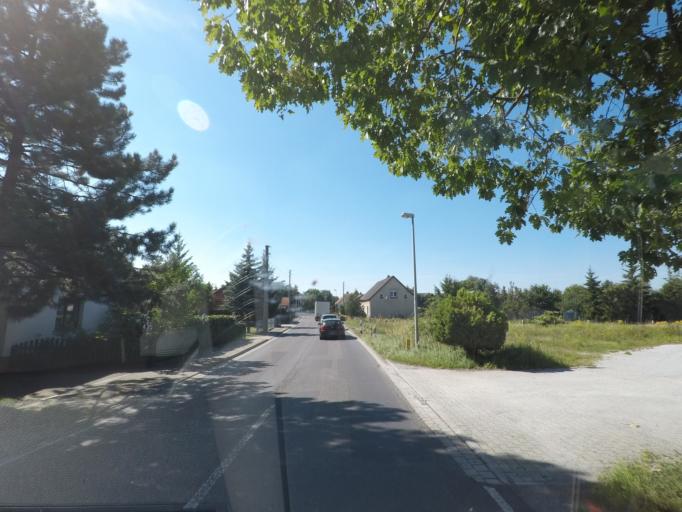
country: DE
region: Brandenburg
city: Welzow
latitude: 51.5566
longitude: 14.1373
